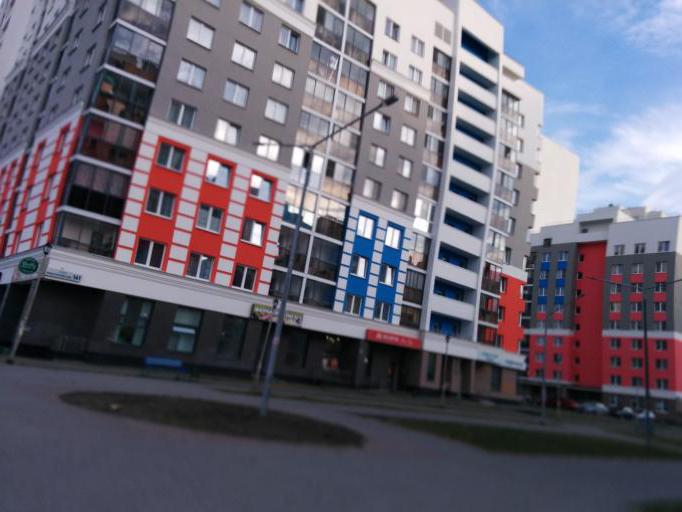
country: RU
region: Sverdlovsk
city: Shirokaya Rechka
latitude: 56.7968
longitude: 60.5145
